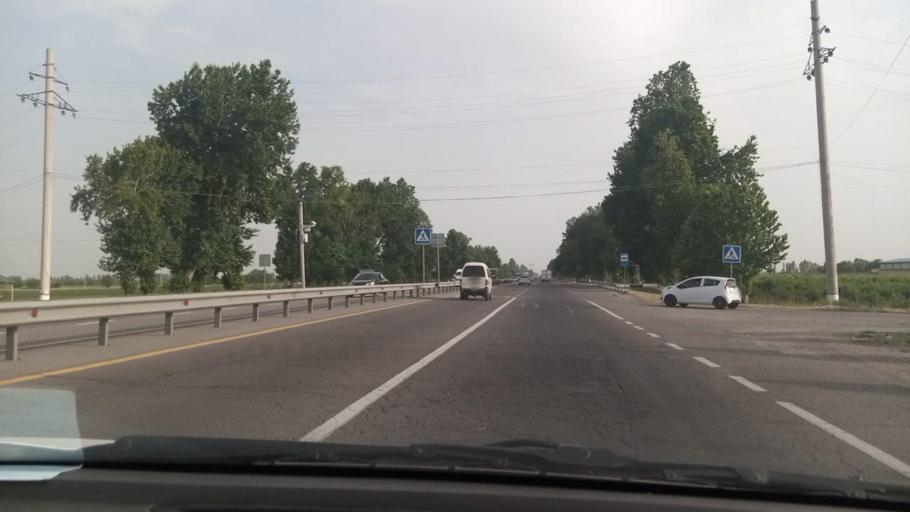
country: UZ
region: Toshkent Shahri
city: Bektemir
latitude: 41.2239
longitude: 69.4024
